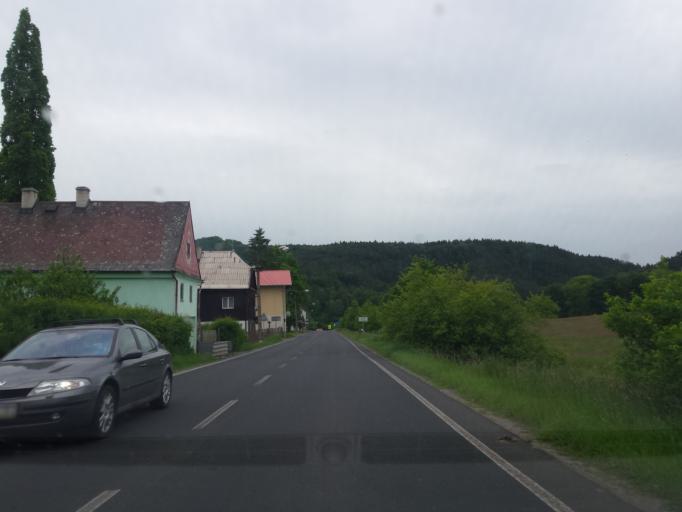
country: CZ
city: Novy Bor
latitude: 50.7412
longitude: 14.5848
